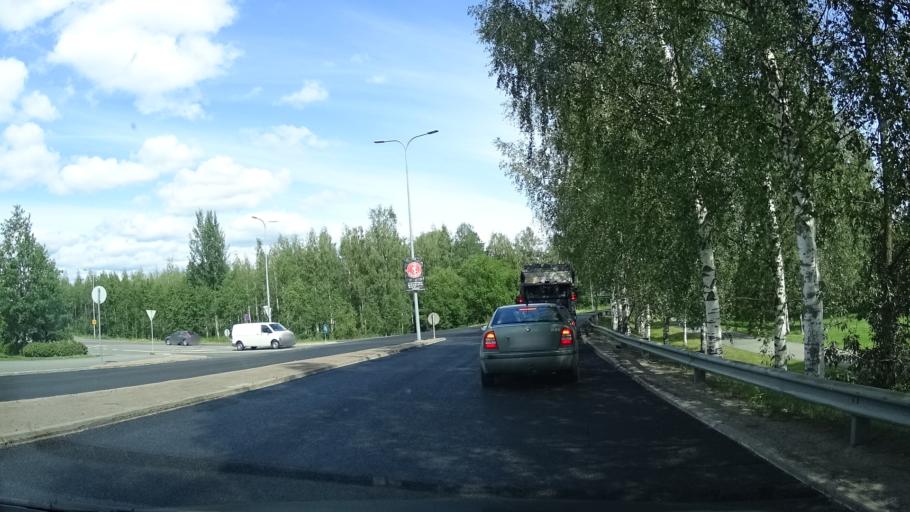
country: FI
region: Central Finland
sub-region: Jyvaeskylae
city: Jyvaeskylae
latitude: 62.2432
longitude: 25.7138
